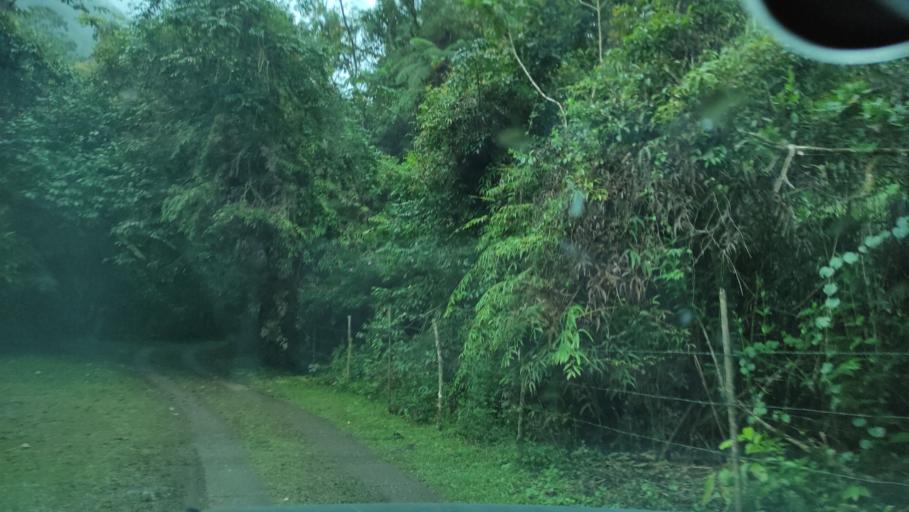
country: CO
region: Valle del Cauca
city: Jamundi
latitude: 3.3188
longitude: -76.6352
